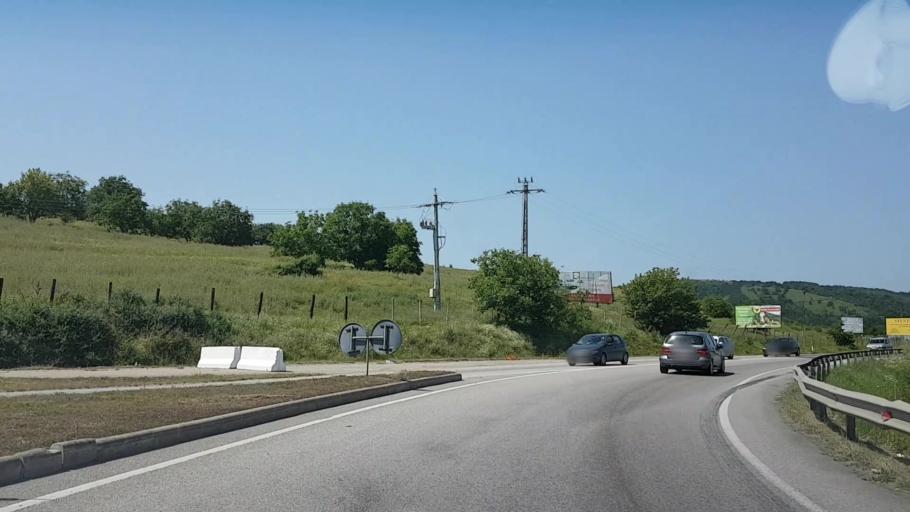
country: RO
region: Cluj
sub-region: Comuna Apahida
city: Apahida
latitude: 46.8225
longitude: 23.7448
